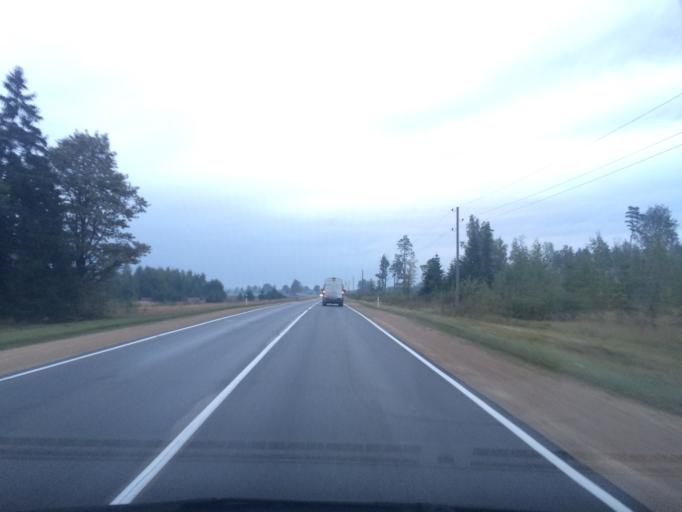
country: LV
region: Salas
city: Sala
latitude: 56.5695
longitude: 25.7758
